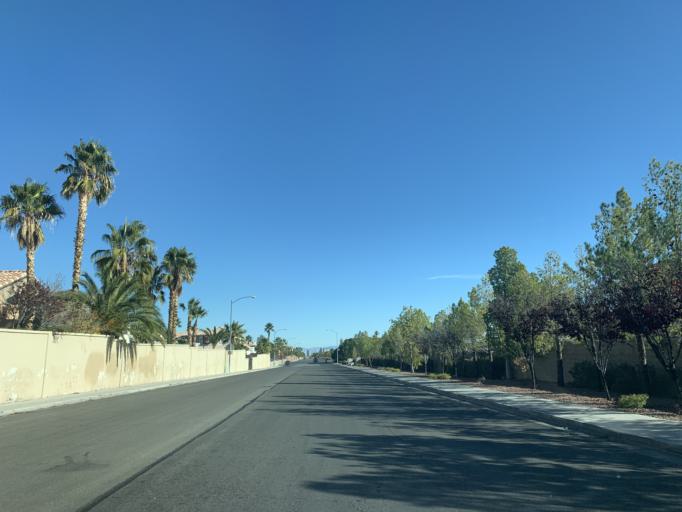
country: US
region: Nevada
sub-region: Clark County
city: Summerlin South
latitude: 36.1168
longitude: -115.2997
